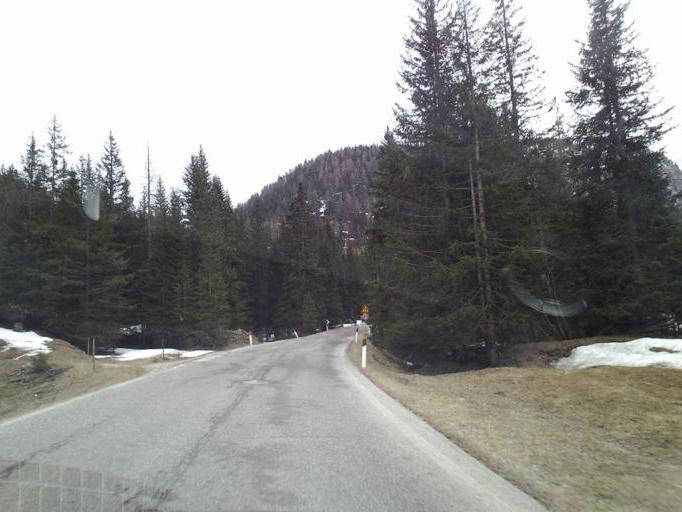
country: IT
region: Veneto
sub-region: Provincia di Belluno
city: Cortina d'Ampezzo
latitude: 46.6035
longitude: 12.2399
